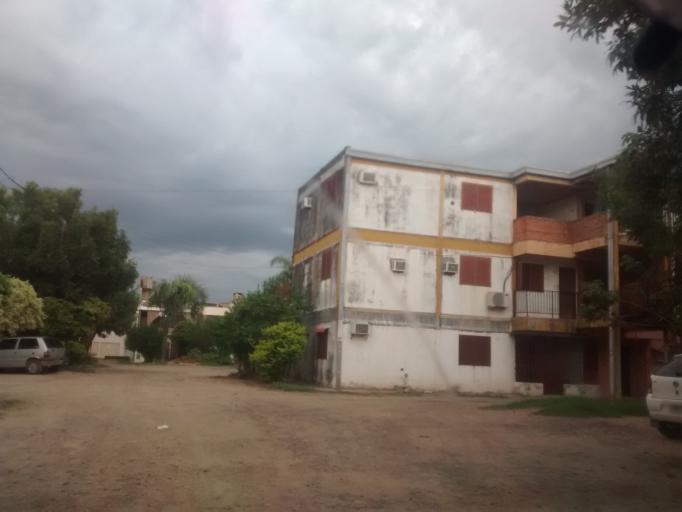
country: AR
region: Chaco
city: Fontana
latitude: -27.4480
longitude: -59.0173
